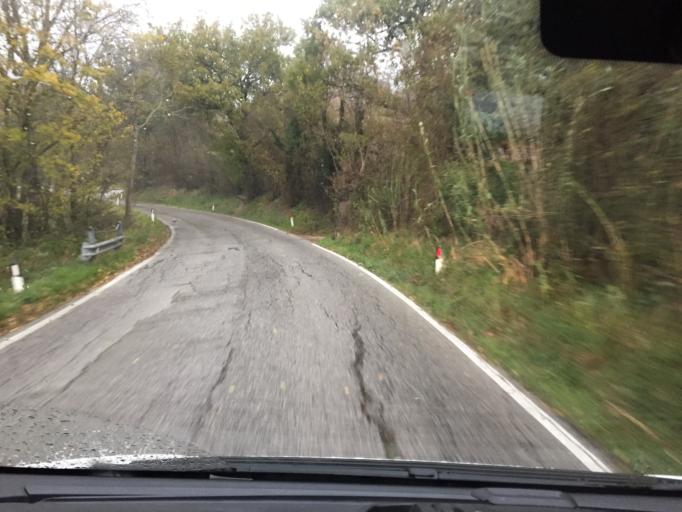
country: IT
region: The Marches
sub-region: Provincia di Macerata
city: Camerino
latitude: 43.1253
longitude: 13.0641
